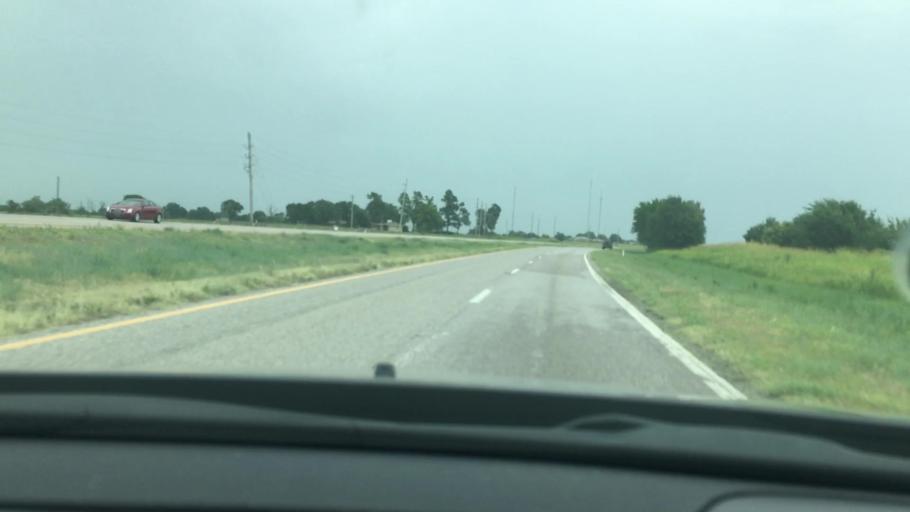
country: US
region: Oklahoma
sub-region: Pontotoc County
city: Ada
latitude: 34.7150
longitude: -96.7253
